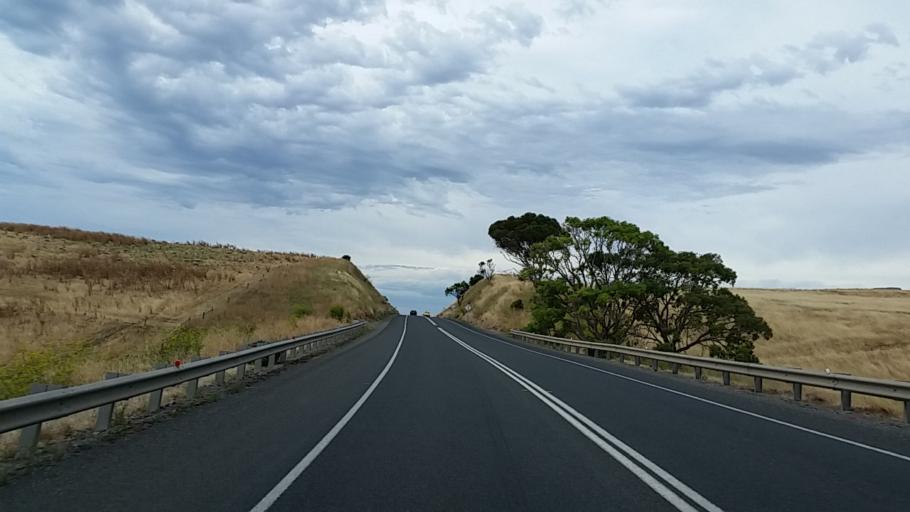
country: AU
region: South Australia
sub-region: Onkaparinga
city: Port Willunga
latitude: -35.3491
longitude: 138.4545
